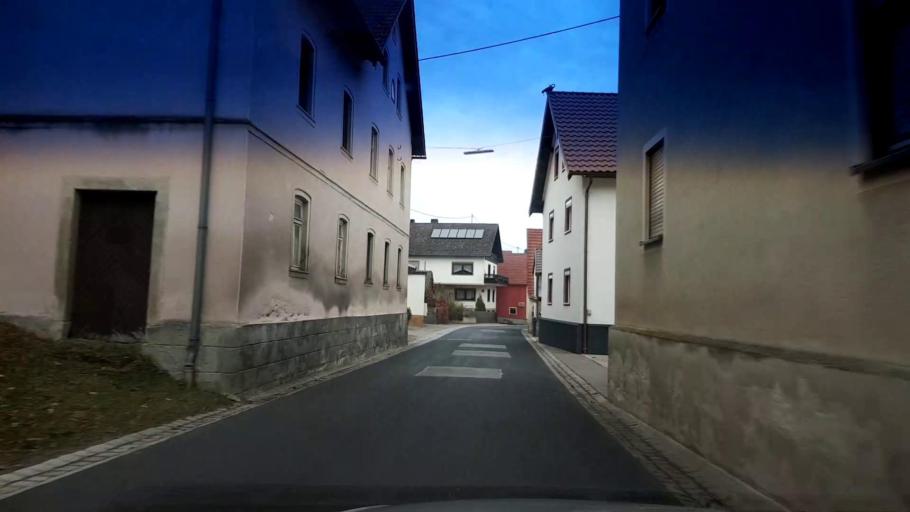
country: DE
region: Bavaria
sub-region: Regierungsbezirk Unterfranken
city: Stettfeld
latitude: 49.9566
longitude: 10.7115
